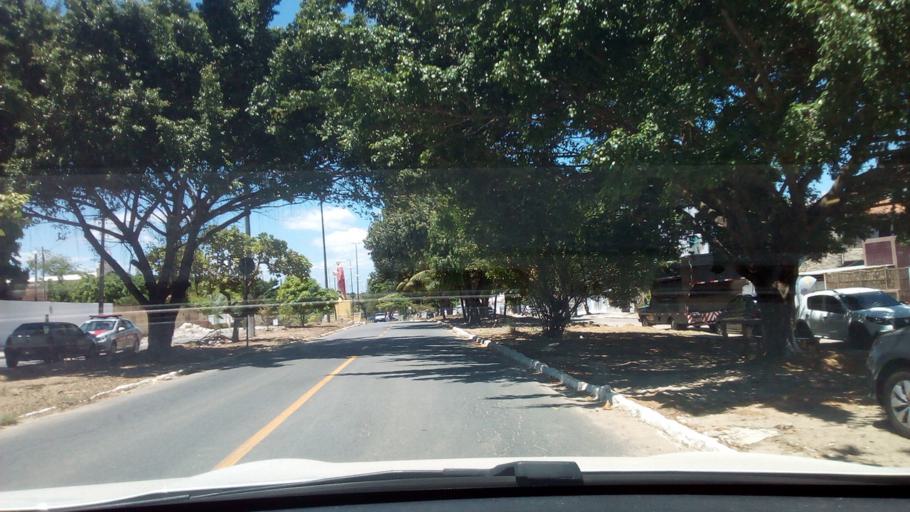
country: BR
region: Paraiba
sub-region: Joao Pessoa
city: Joao Pessoa
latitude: -7.1485
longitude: -34.8338
